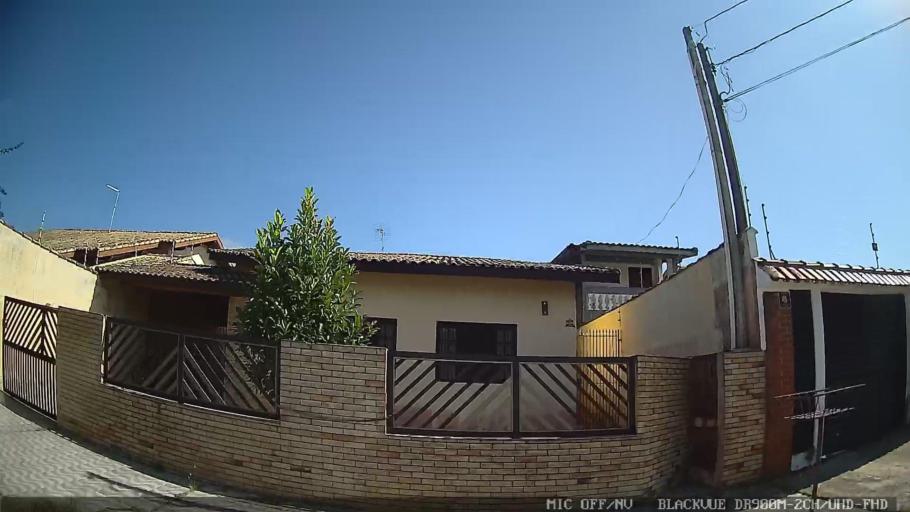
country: BR
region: Sao Paulo
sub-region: Peruibe
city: Peruibe
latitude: -24.3065
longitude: -46.9902
